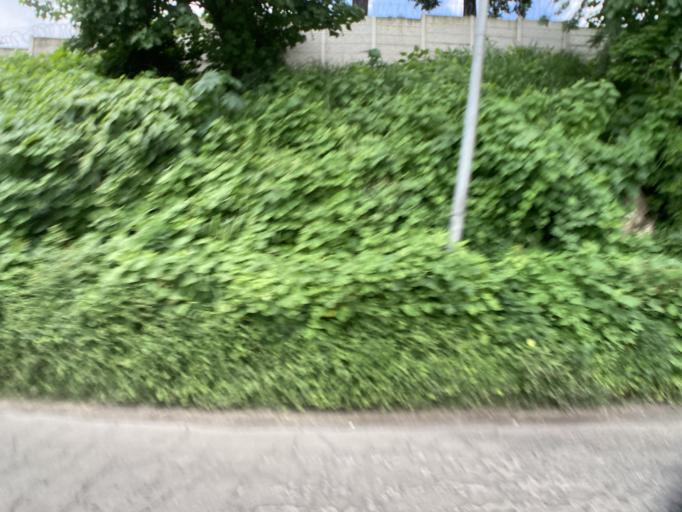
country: GT
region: Guatemala
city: Amatitlan
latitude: 14.4638
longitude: -90.5876
